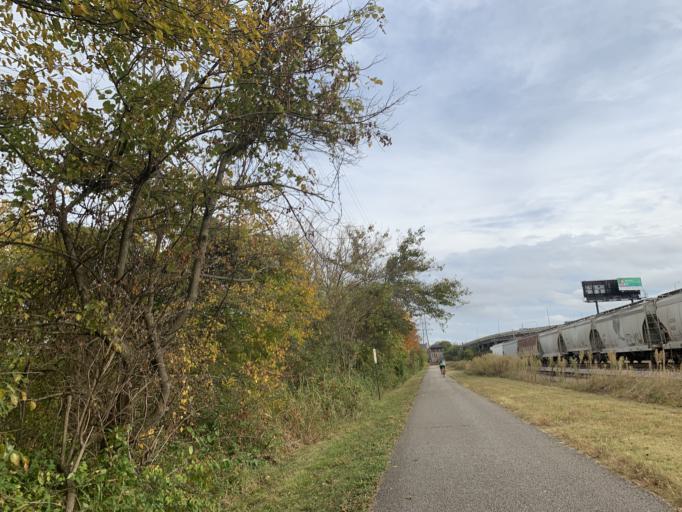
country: US
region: Kentucky
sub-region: Jefferson County
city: Louisville
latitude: 38.2660
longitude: -85.7751
